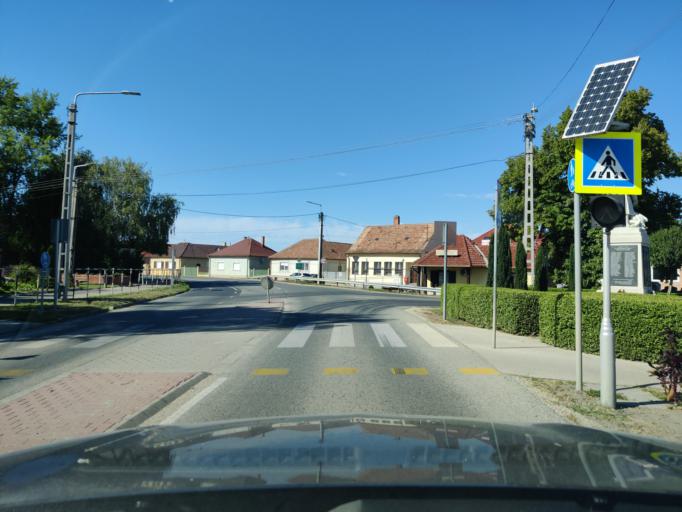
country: HU
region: Gyor-Moson-Sopron
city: Bosarkany
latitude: 47.6887
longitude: 17.2516
